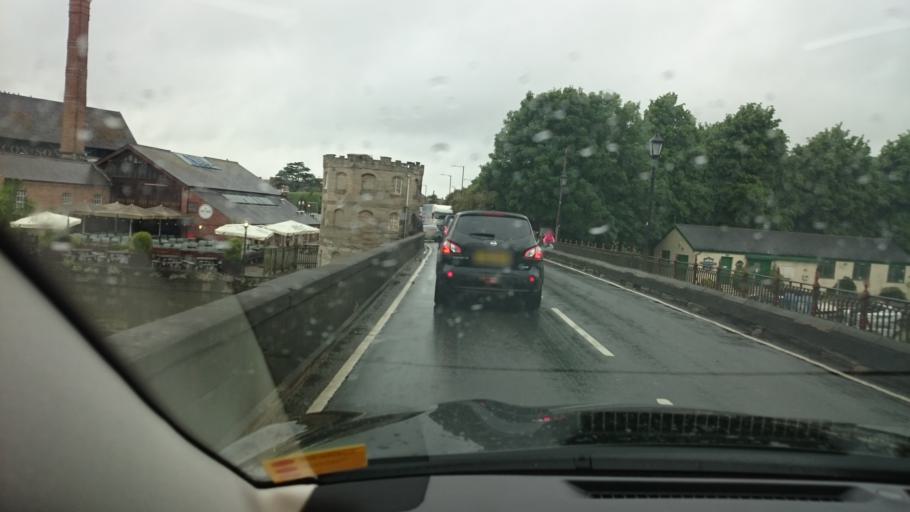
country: GB
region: England
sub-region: Warwickshire
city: Stratford-upon-Avon
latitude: 52.1917
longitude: -1.7006
